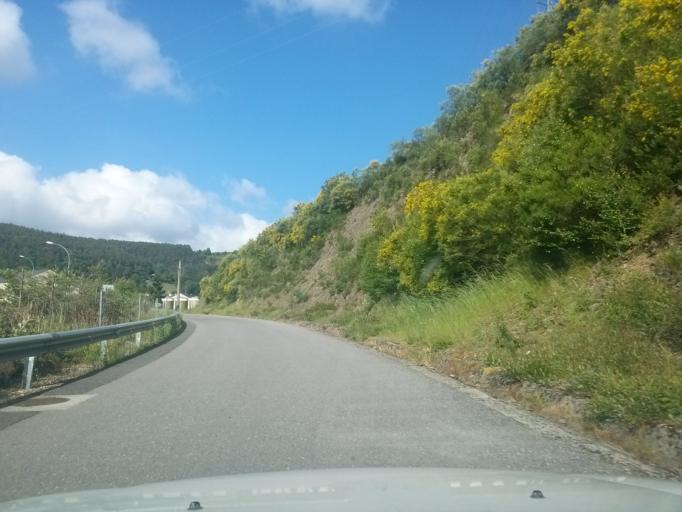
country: ES
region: Castille and Leon
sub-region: Provincia de Leon
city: Balboa
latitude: 42.7248
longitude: -7.0267
